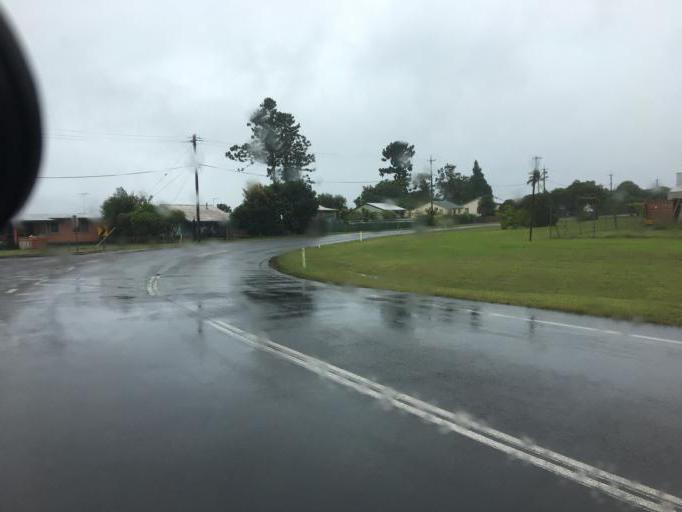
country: AU
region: Queensland
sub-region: Tablelands
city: Tolga
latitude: -17.2160
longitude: 145.5381
